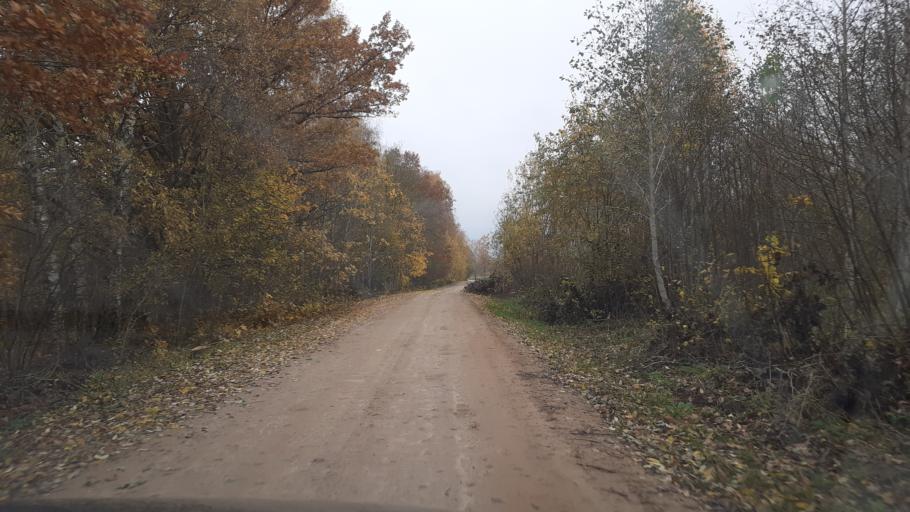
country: LV
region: Saldus Rajons
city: Saldus
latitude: 56.8768
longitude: 22.3000
